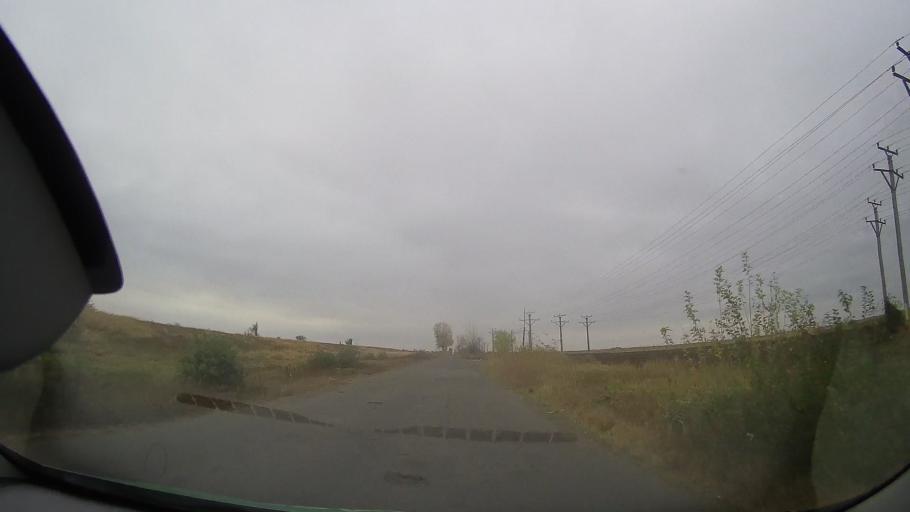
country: RO
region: Braila
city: Dudesti
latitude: 44.9111
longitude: 27.4306
